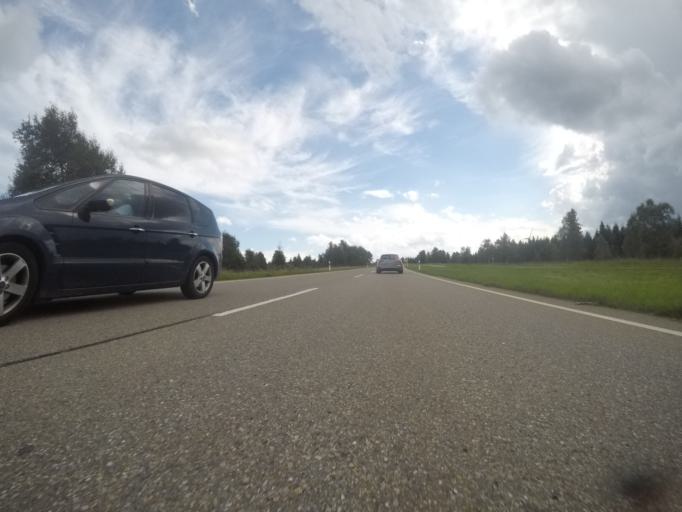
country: DE
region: Baden-Wuerttemberg
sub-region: Freiburg Region
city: Bad Peterstal-Griesbach
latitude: 48.4845
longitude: 8.2743
